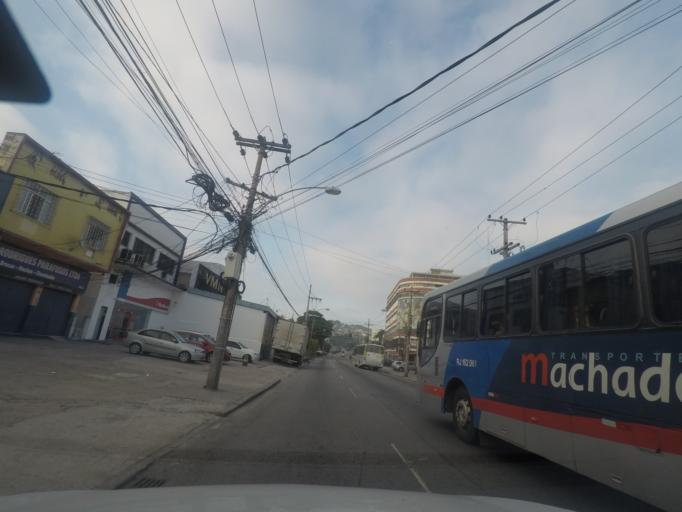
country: BR
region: Rio de Janeiro
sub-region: Duque De Caxias
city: Duque de Caxias
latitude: -22.8338
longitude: -43.2809
